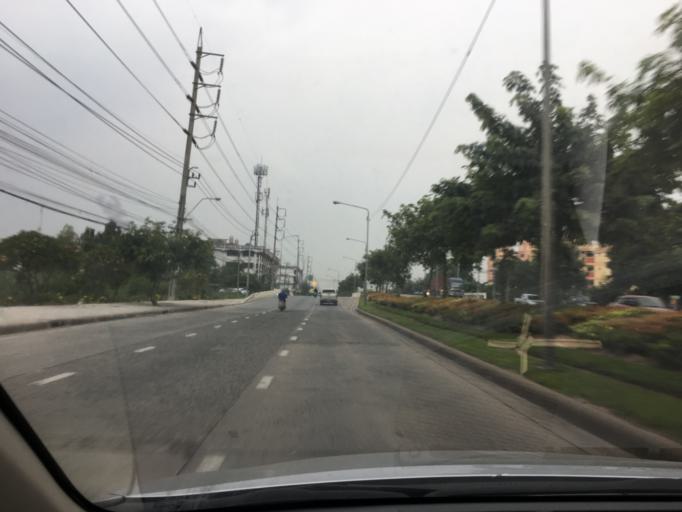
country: TH
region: Bangkok
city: Lat Krabang
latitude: 13.7524
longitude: 100.7784
